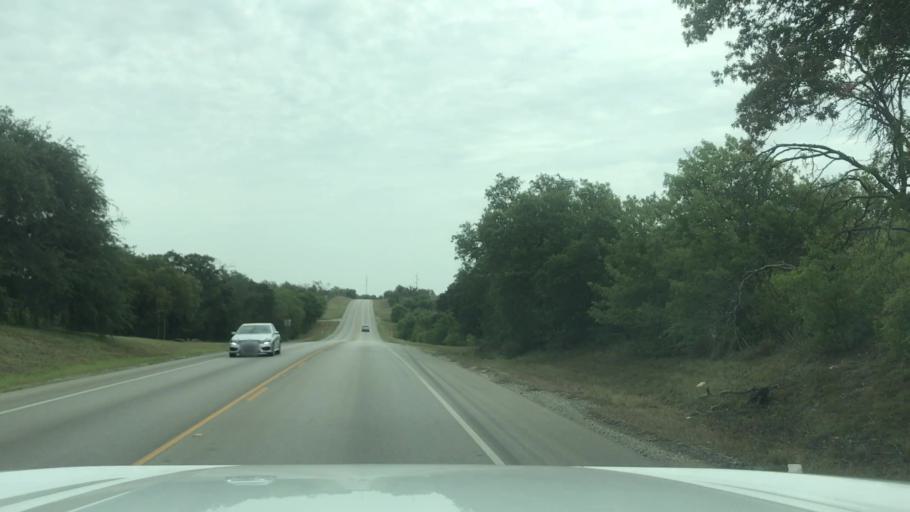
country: US
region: Texas
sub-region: Erath County
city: Dublin
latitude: 32.0980
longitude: -98.3889
